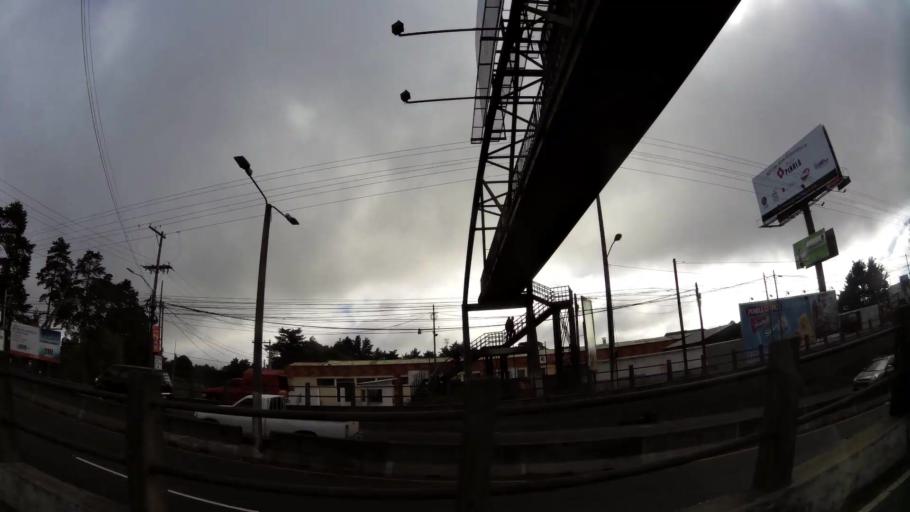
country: GT
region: Guatemala
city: San Jose Pinula
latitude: 14.5436
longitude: -90.4542
